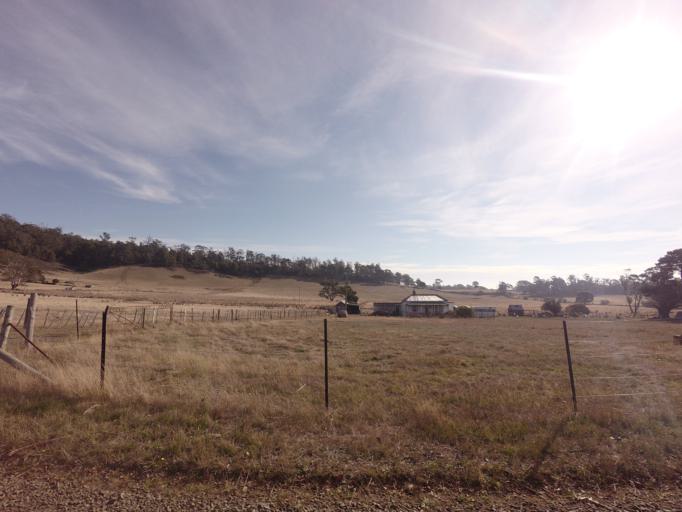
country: AU
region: Tasmania
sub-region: Sorell
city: Sorell
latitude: -42.4812
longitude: 147.4804
